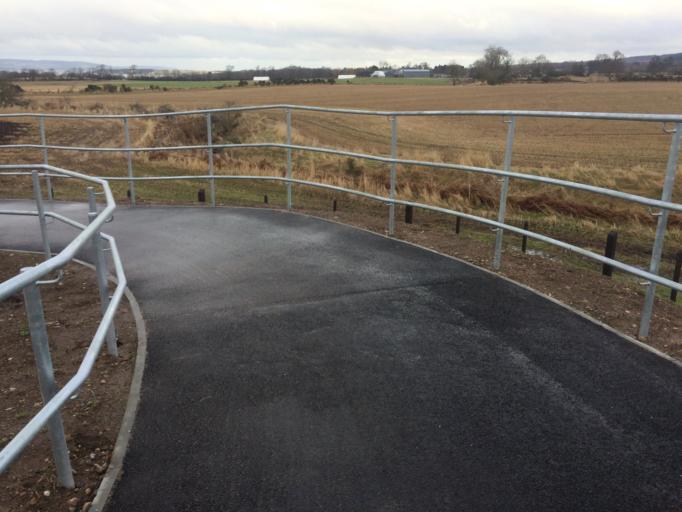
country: GB
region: Scotland
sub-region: Highland
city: Inverness
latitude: 57.4771
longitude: -4.1747
